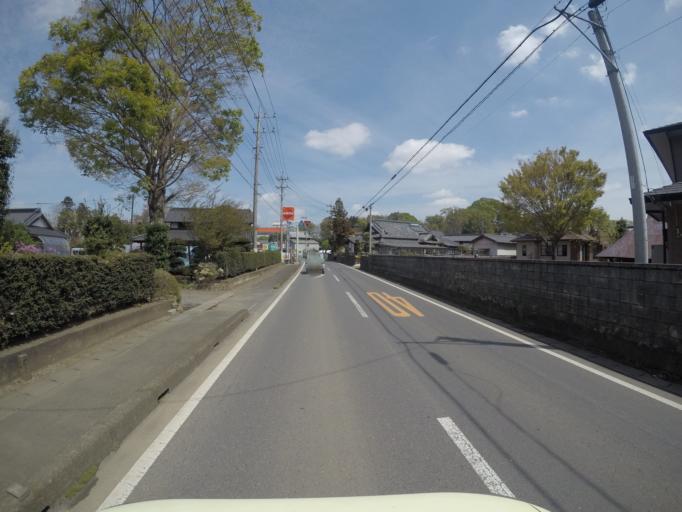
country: JP
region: Ibaraki
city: Shimodate
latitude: 36.2896
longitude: 140.0341
